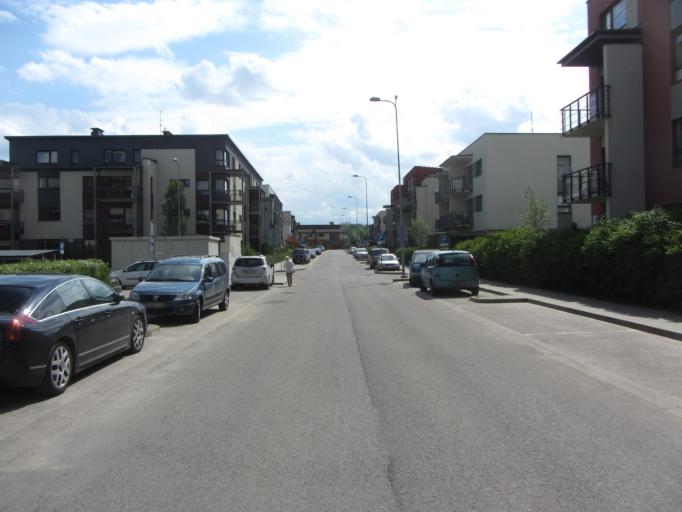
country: LT
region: Vilnius County
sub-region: Vilnius
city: Fabijoniskes
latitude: 54.7625
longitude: 25.2840
